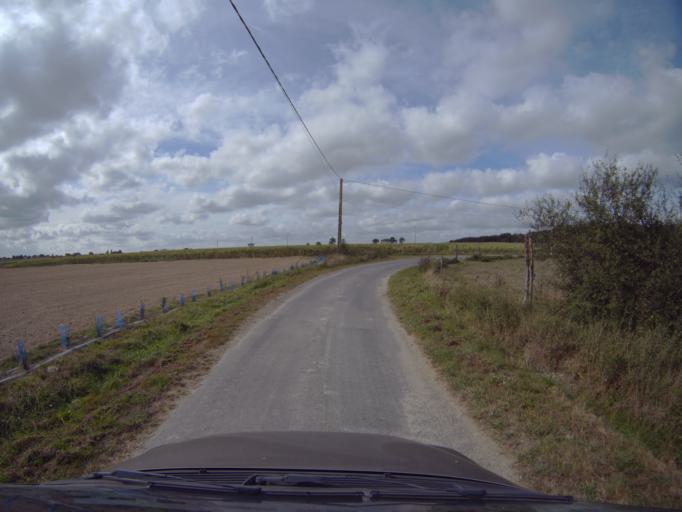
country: FR
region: Pays de la Loire
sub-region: Departement de la Loire-Atlantique
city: La Planche
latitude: 47.0368
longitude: -1.4066
